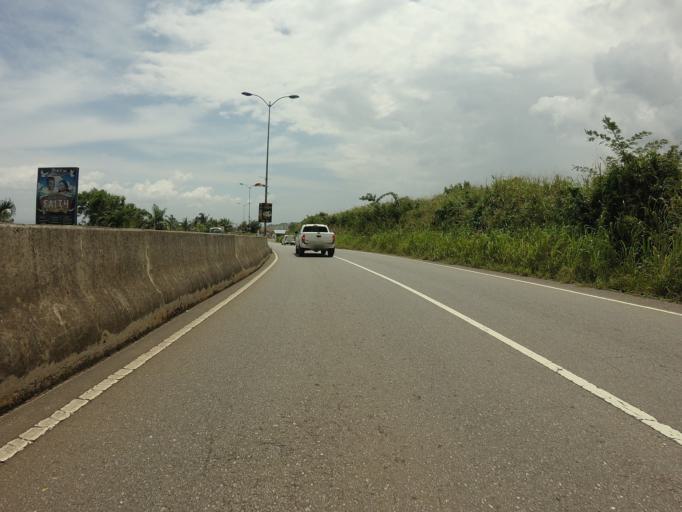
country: GH
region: Eastern
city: Aburi
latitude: 5.8024
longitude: -0.1819
